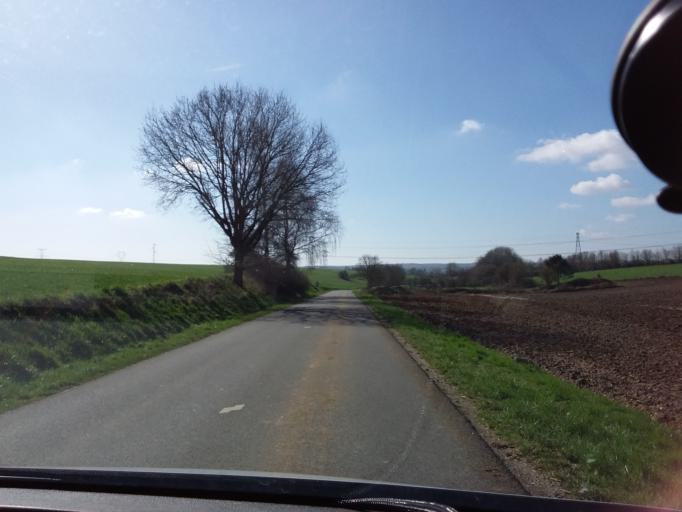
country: FR
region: Picardie
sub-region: Departement de l'Aisne
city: Hirson
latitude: 49.8890
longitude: 4.0981
